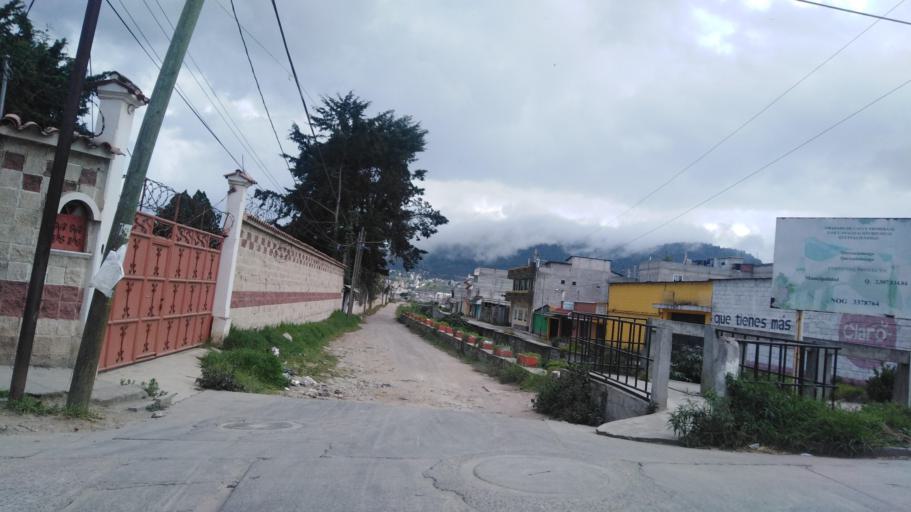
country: GT
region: Quetzaltenango
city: Quetzaltenango
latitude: 14.8491
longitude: -91.5120
